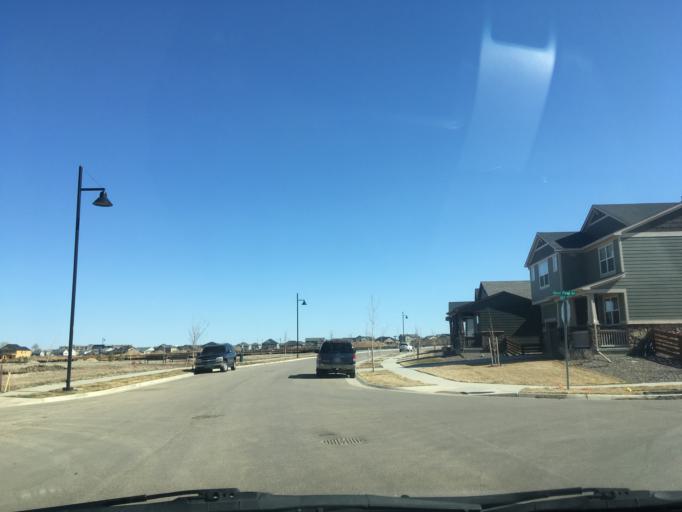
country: US
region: Colorado
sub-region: Boulder County
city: Erie
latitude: 40.0544
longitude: -105.0343
